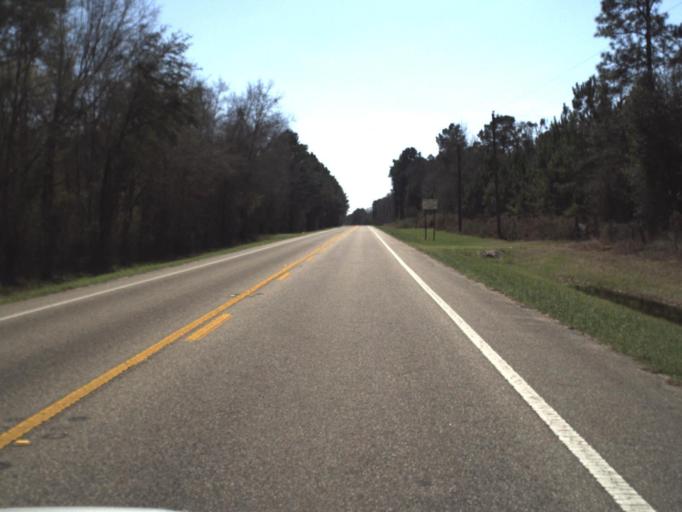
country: US
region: Florida
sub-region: Calhoun County
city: Blountstown
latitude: 30.5445
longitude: -85.0265
